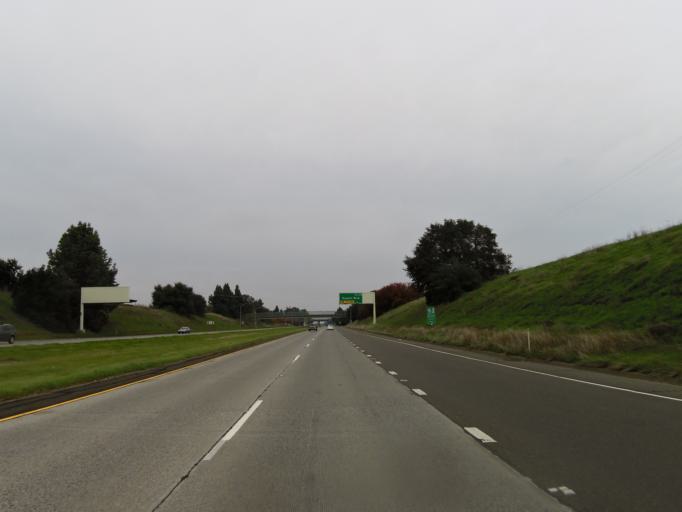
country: US
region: California
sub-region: Yolo County
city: Davis
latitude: 38.5408
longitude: -121.7682
